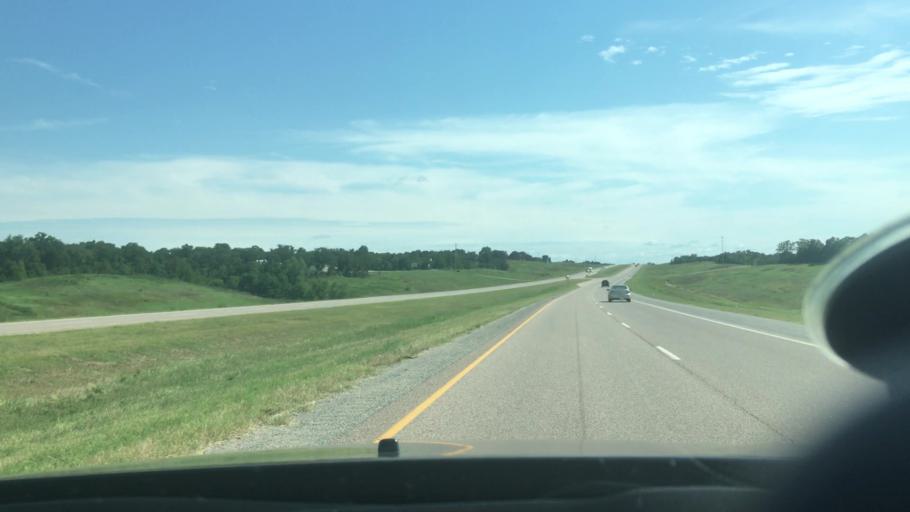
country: US
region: Oklahoma
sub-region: Pontotoc County
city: Byng
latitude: 34.8873
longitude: -96.6754
